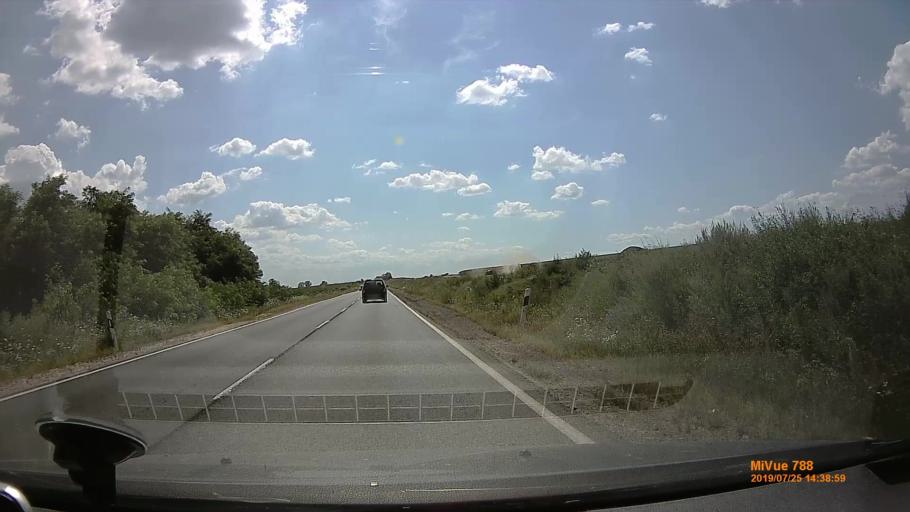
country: HU
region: Borsod-Abauj-Zemplen
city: Halmaj
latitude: 48.3026
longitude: 21.0589
